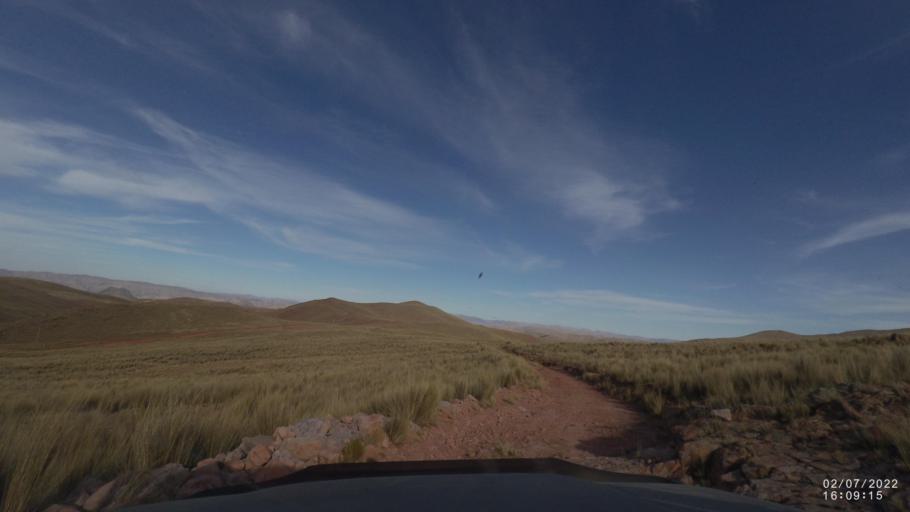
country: BO
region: Cochabamba
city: Irpa Irpa
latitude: -17.9101
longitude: -66.4441
